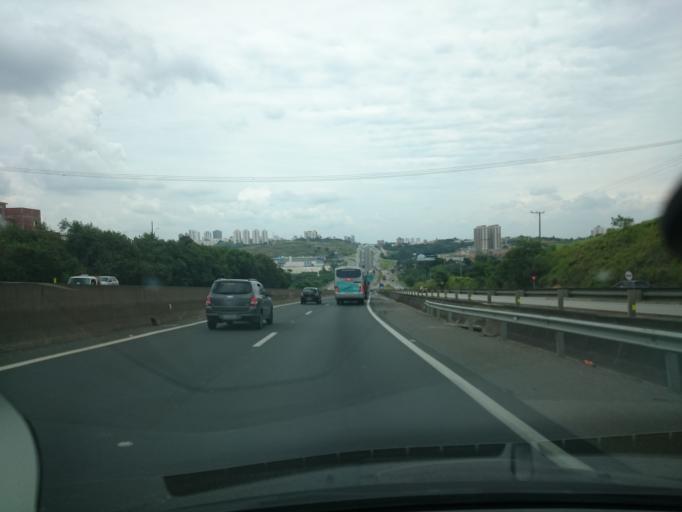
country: BR
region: Sao Paulo
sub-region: Votorantim
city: Votorantim
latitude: -23.5250
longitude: -47.4419
